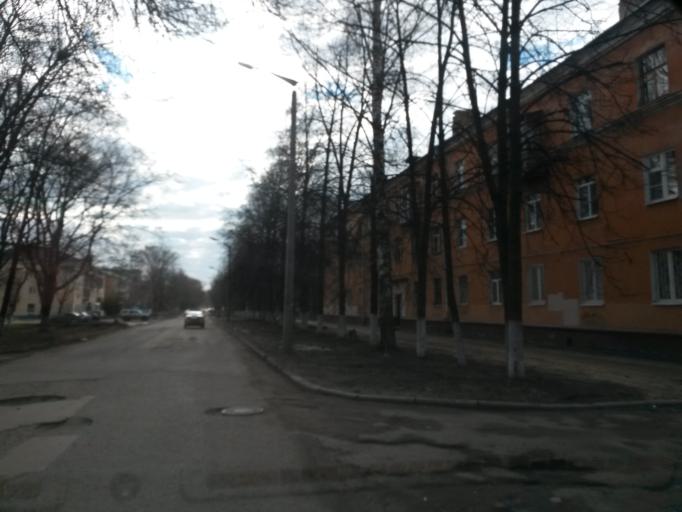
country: RU
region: Jaroslavl
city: Yaroslavl
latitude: 57.6357
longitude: 39.8384
